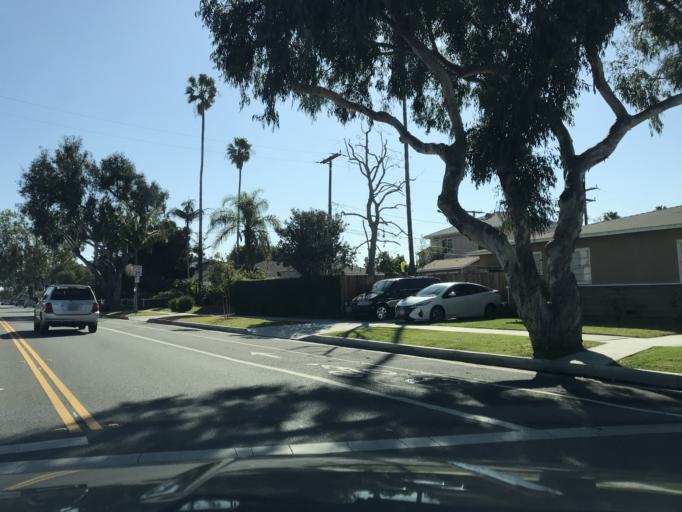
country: US
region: California
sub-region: Orange County
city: Huntington Beach
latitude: 33.6720
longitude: -117.9980
